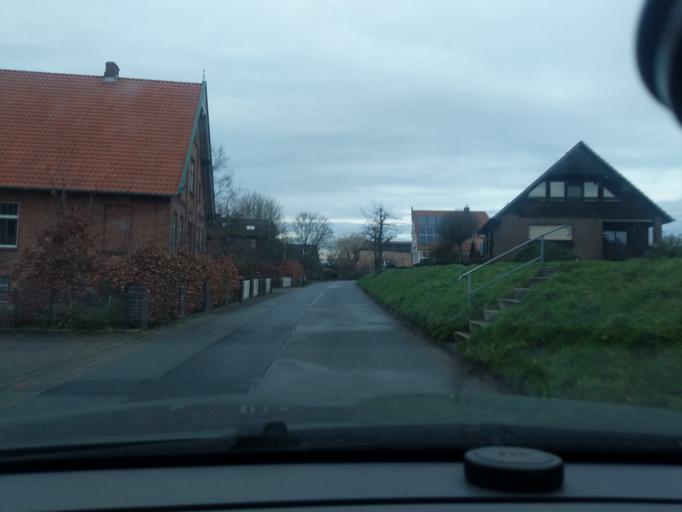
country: DE
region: Lower Saxony
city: Neuenkirchen
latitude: 53.5287
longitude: 9.6048
